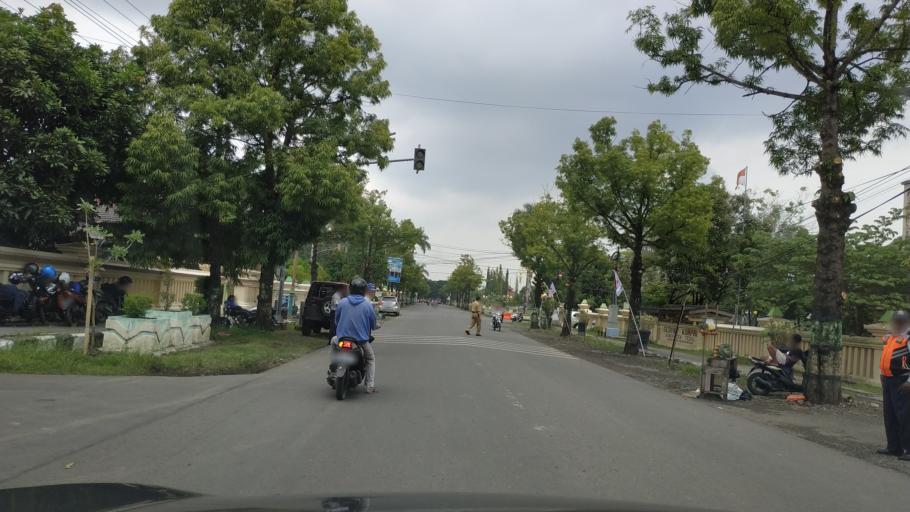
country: ID
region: Central Java
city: Slawi
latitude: -6.9938
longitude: 109.1299
